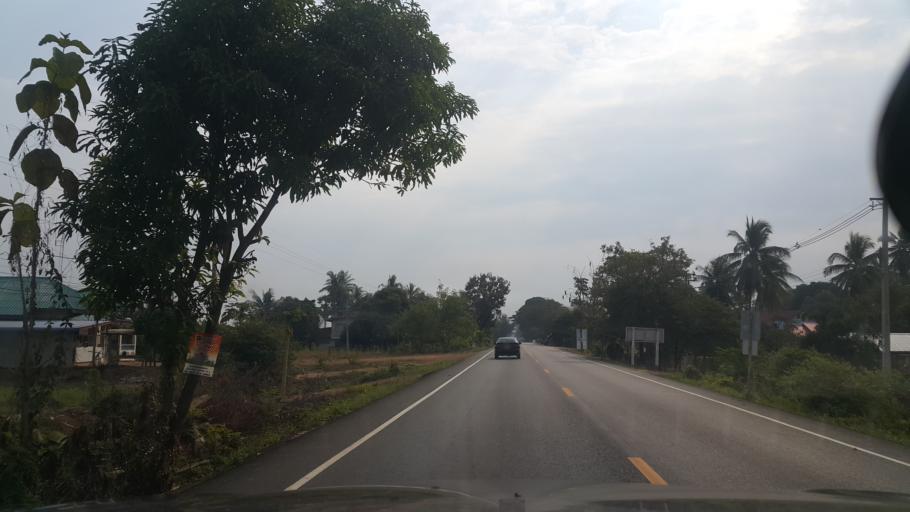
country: TH
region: Sukhothai
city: Si Samrong
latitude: 17.1801
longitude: 99.8394
